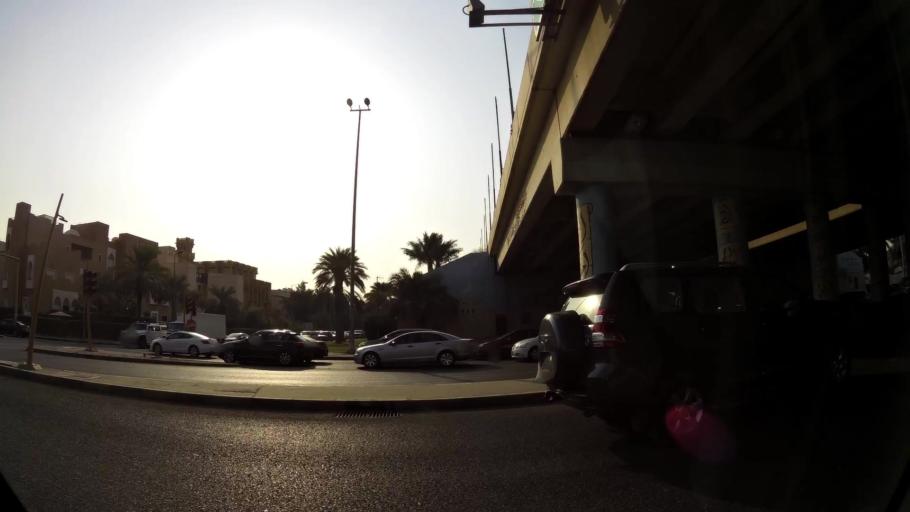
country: KW
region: Muhafazat Hawalli
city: Salwa
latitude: 29.2936
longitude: 48.0695
